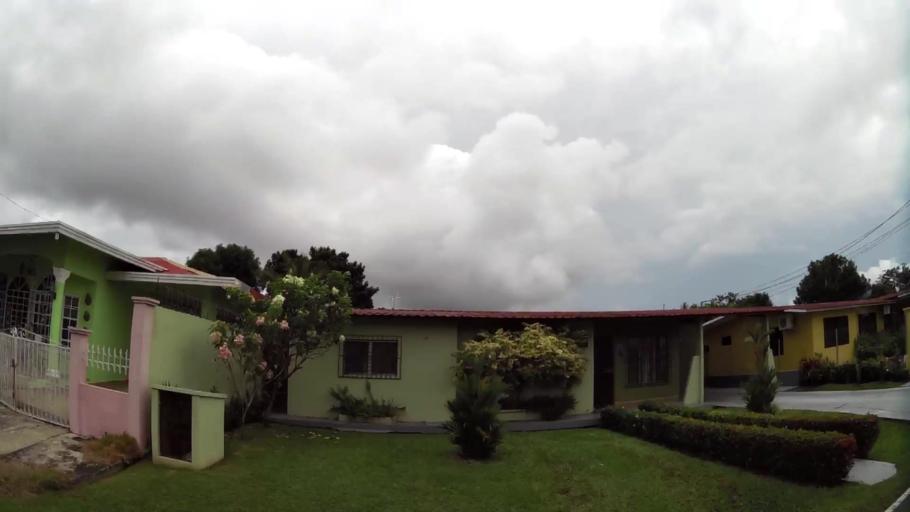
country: PA
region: Chiriqui
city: David
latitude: 8.4185
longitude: -82.4543
